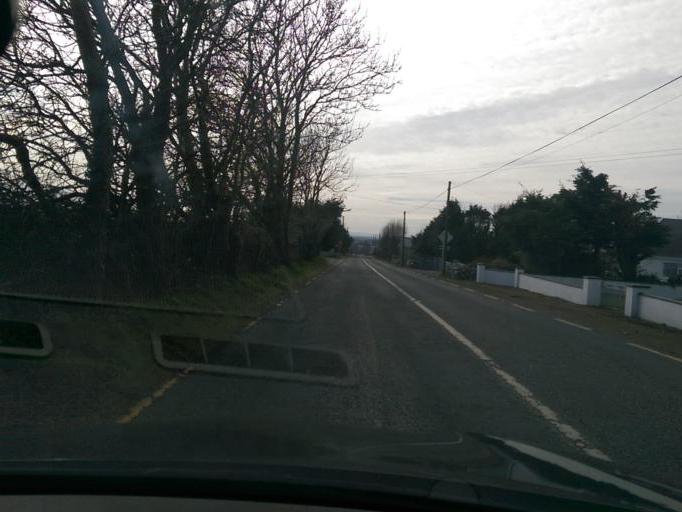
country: IE
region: Connaught
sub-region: County Galway
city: Tuam
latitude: 53.4059
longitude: -8.8240
